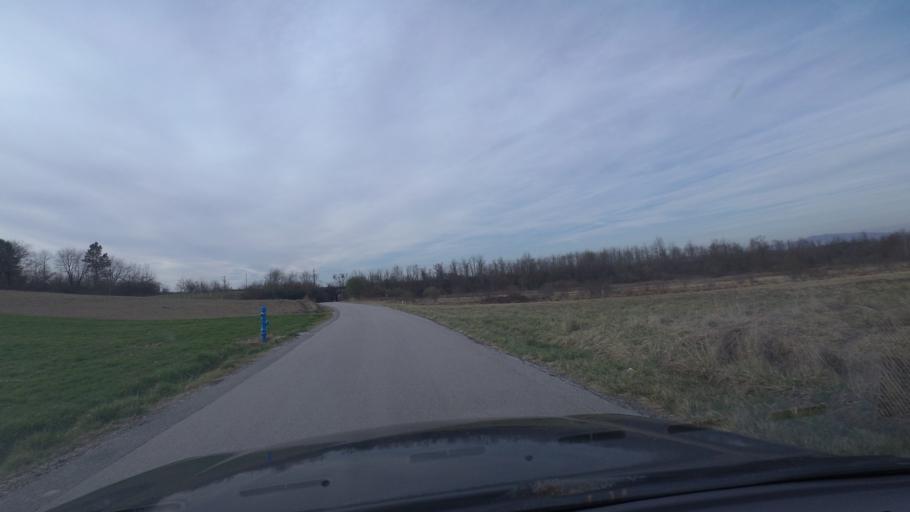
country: HR
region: Grad Zagreb
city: Horvati
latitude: 45.7145
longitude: 15.8241
